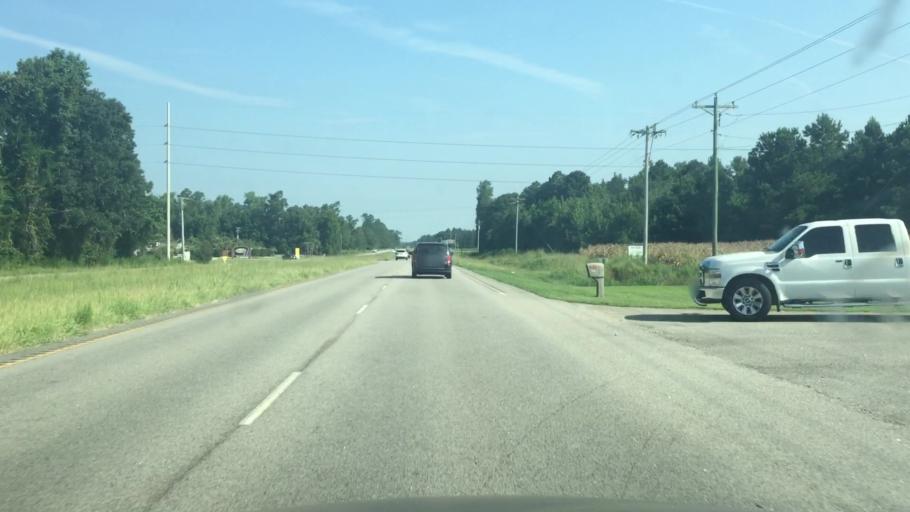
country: US
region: South Carolina
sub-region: Horry County
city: Little River
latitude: 33.9642
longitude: -78.7386
